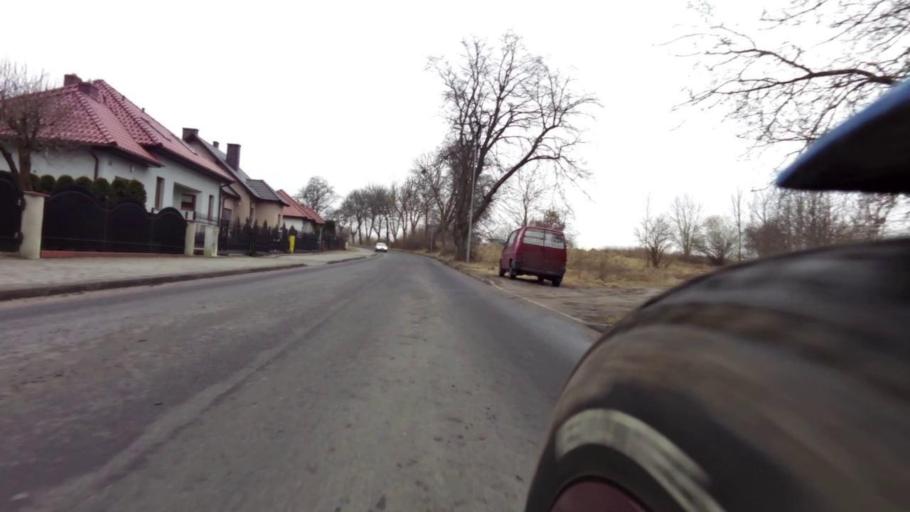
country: PL
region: West Pomeranian Voivodeship
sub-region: Powiat walecki
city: Walcz
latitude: 53.2665
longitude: 16.4846
